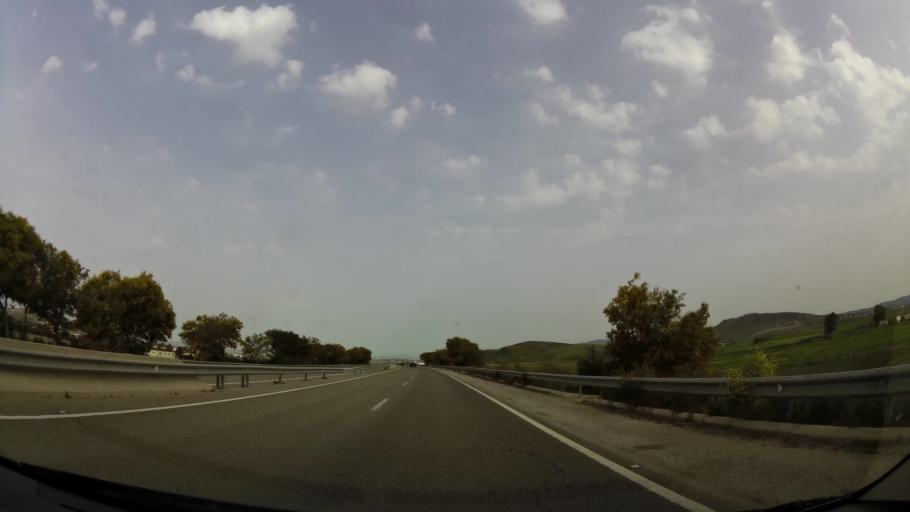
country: MA
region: Tanger-Tetouan
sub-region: Tanger-Assilah
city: Boukhalef
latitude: 35.6534
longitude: -5.8704
